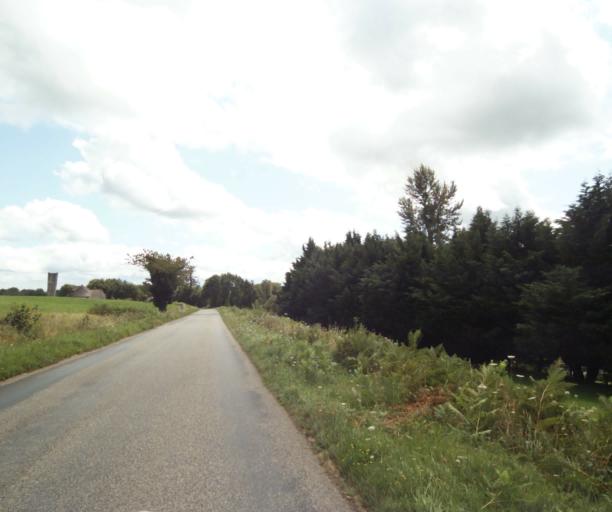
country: FR
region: Limousin
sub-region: Departement de la Correze
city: Sainte-Fortunade
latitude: 45.1919
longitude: 1.8111
